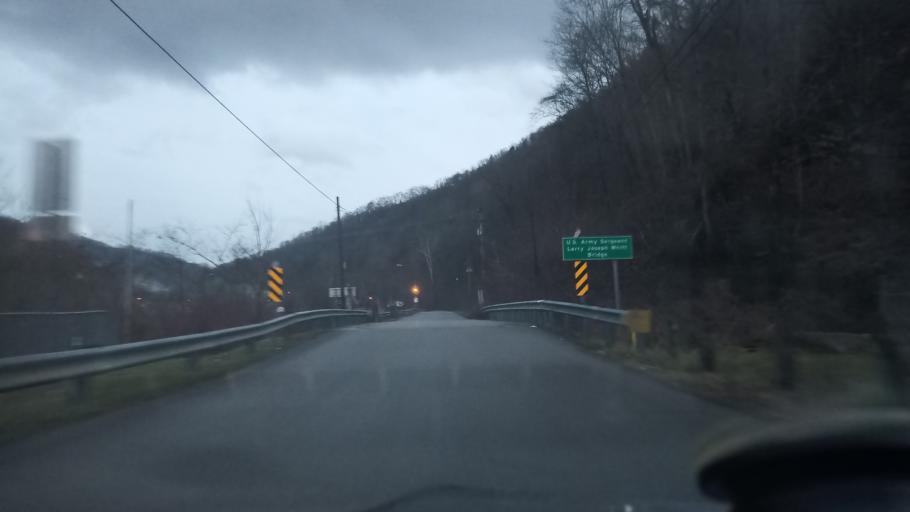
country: US
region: West Virginia
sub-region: Logan County
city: Mallory
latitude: 37.7296
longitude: -81.8776
